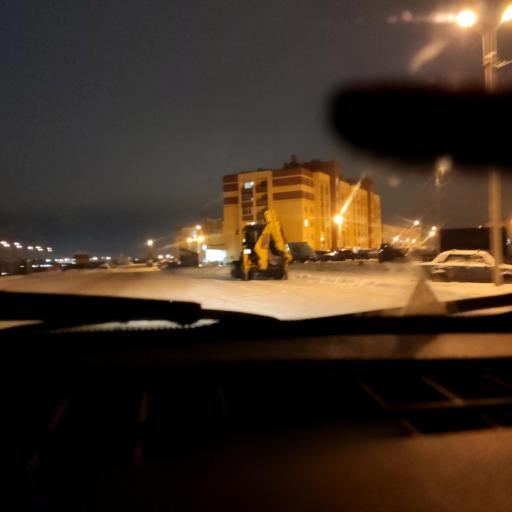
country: RU
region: Bashkortostan
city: Ufa
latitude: 54.6241
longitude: 55.8826
